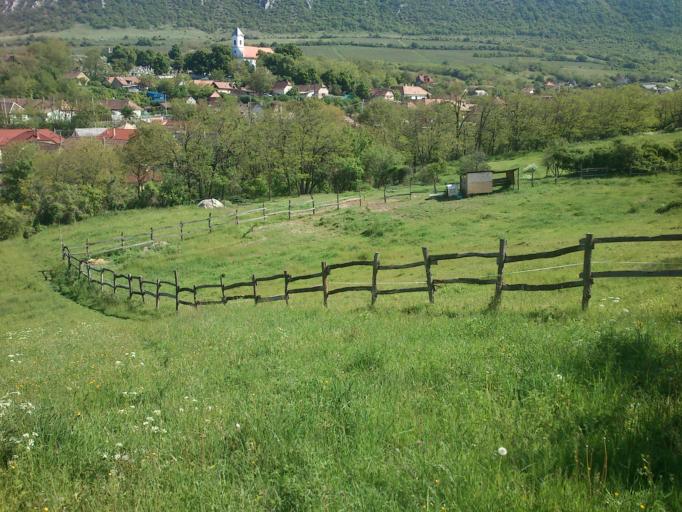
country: HU
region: Komarom-Esztergom
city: Kesztolc
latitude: 47.7104
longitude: 18.7967
